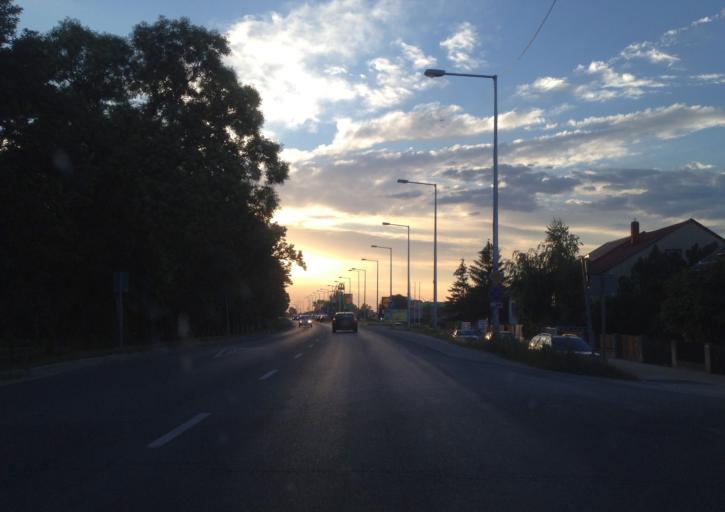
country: HU
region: Gyor-Moson-Sopron
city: Mosonmagyarovar
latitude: 47.8753
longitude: 17.2638
